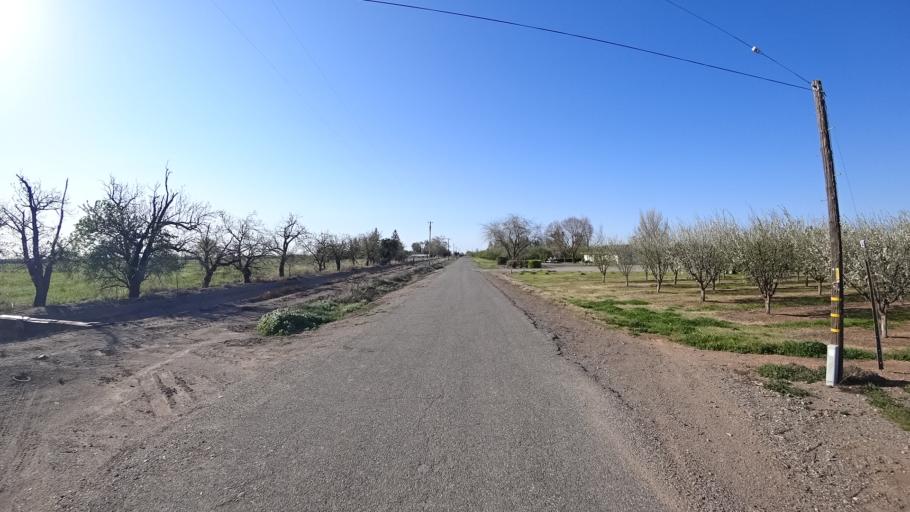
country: US
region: California
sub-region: Glenn County
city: Orland
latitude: 39.7656
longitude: -122.1227
